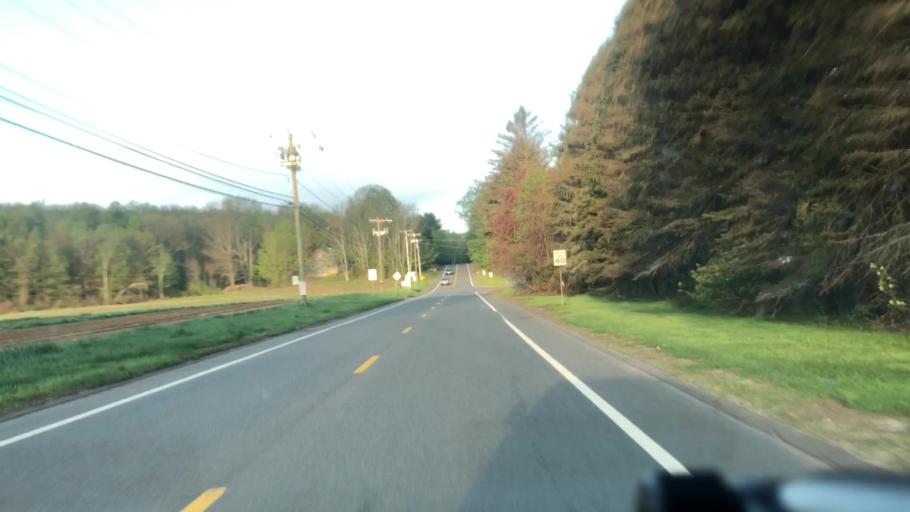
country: US
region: Massachusetts
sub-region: Hampshire County
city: Westhampton
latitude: 42.2858
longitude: -72.7731
